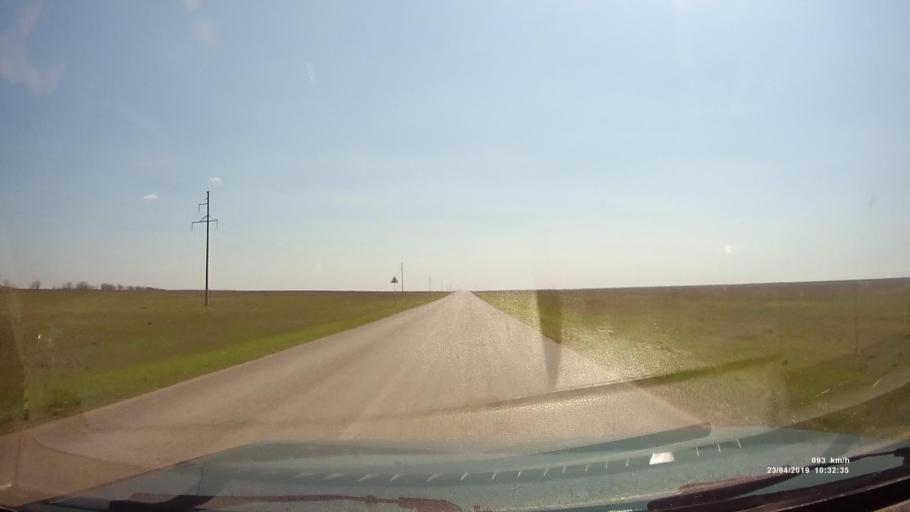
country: RU
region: Kalmykiya
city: Yashalta
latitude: 46.5793
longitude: 42.5803
